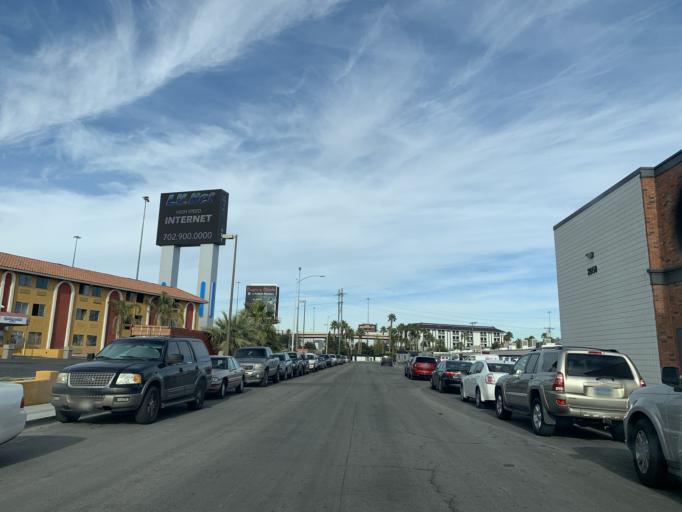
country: US
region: Nevada
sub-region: Clark County
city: Las Vegas
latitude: 36.1419
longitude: -115.1715
